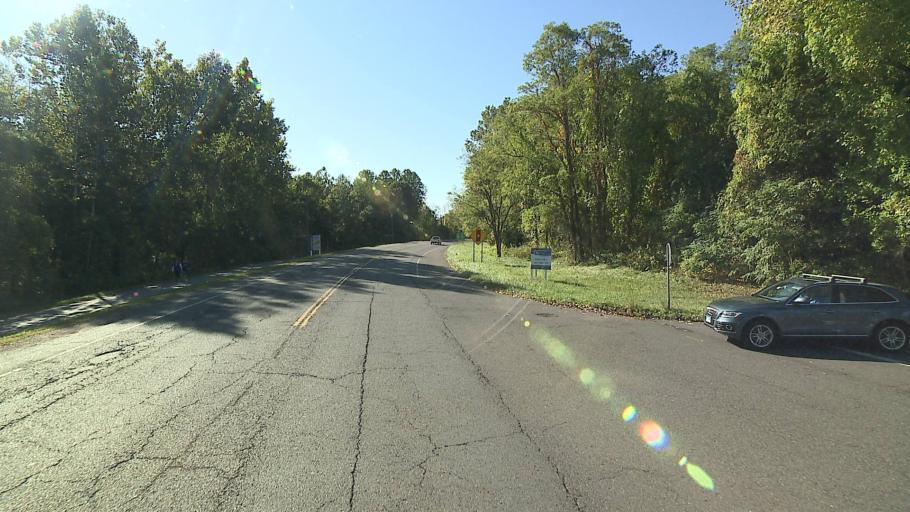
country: US
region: Connecticut
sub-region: Fairfield County
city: Danbury
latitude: 41.4759
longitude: -73.4073
